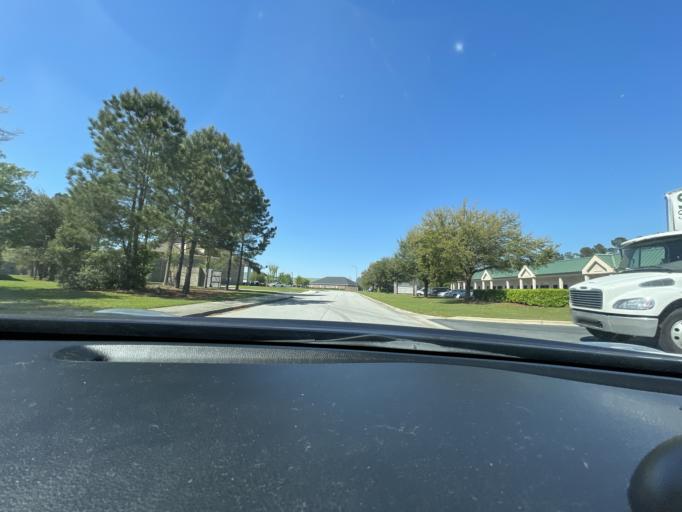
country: US
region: Georgia
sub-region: Chatham County
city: Pooler
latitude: 32.1315
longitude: -81.2535
